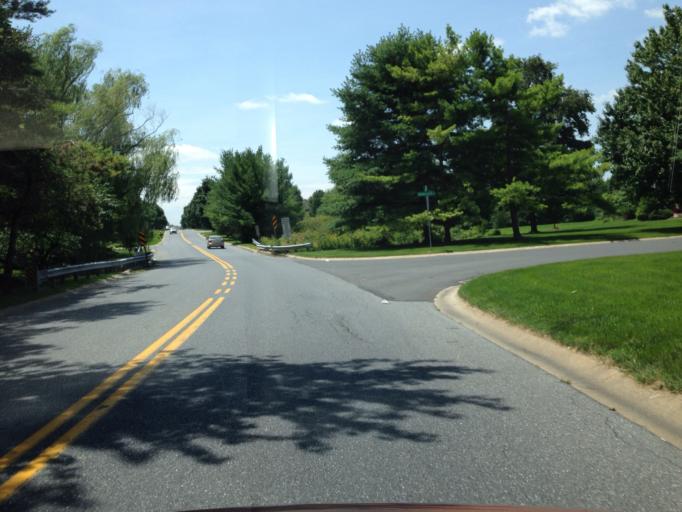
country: US
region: Pennsylvania
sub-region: Lancaster County
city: East Petersburg
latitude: 40.1109
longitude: -76.3272
